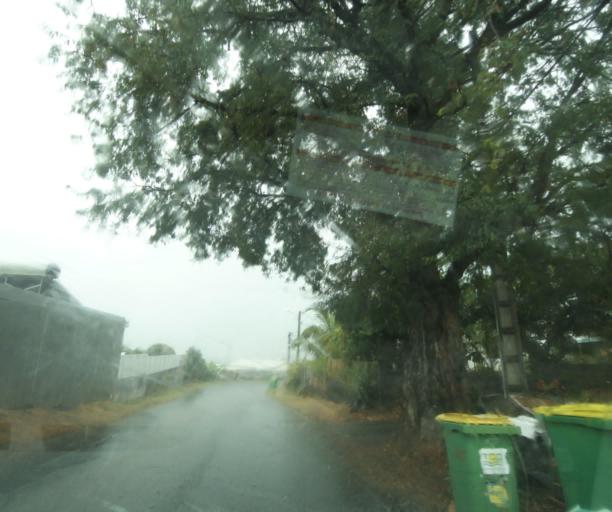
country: RE
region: Reunion
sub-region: Reunion
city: Saint-Paul
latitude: -20.9867
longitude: 55.3238
